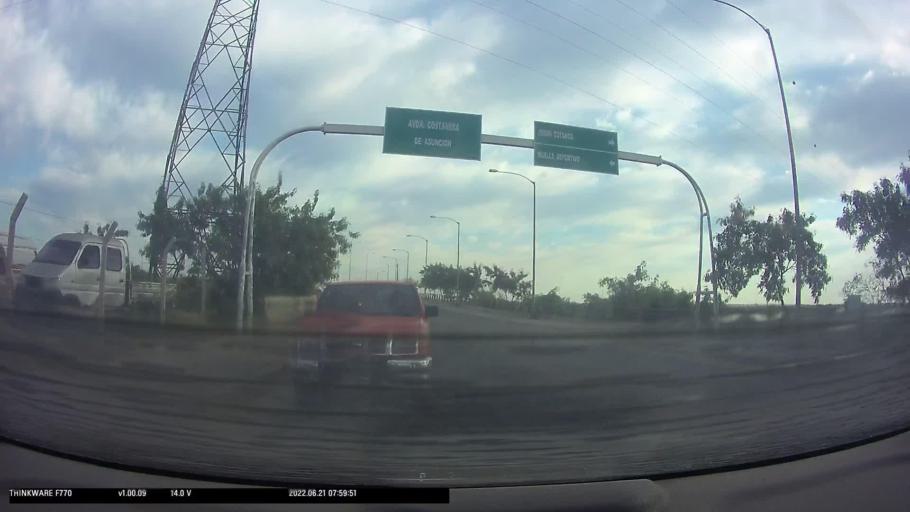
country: PY
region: Asuncion
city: Asuncion
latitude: -25.2728
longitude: -57.6118
